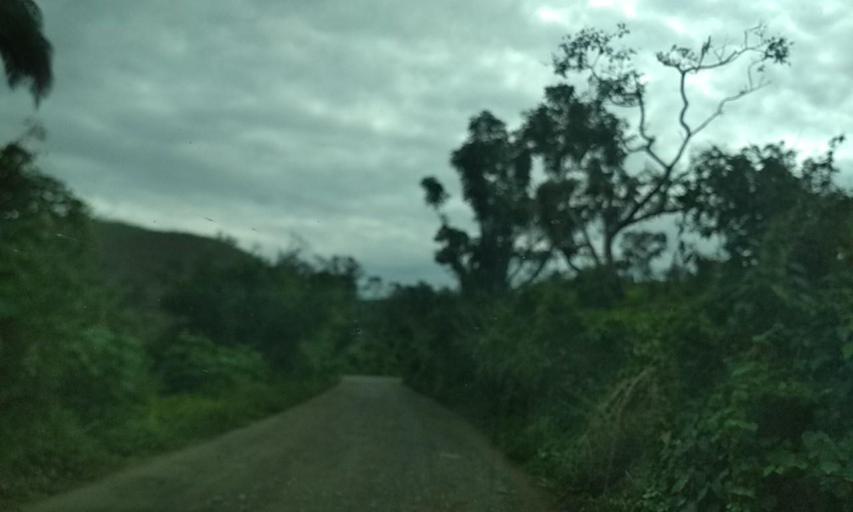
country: MX
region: Veracruz
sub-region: Papantla
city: Residencial Tajin
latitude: 20.6302
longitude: -97.3648
